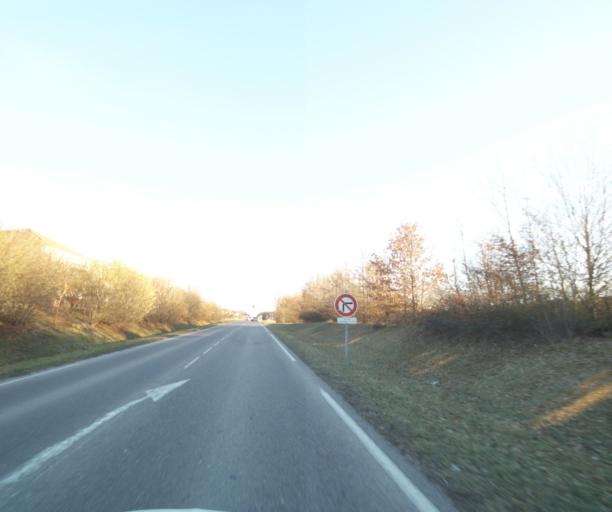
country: FR
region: Lorraine
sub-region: Departement de Meurthe-et-Moselle
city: Tomblaine
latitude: 48.6772
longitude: 6.2262
